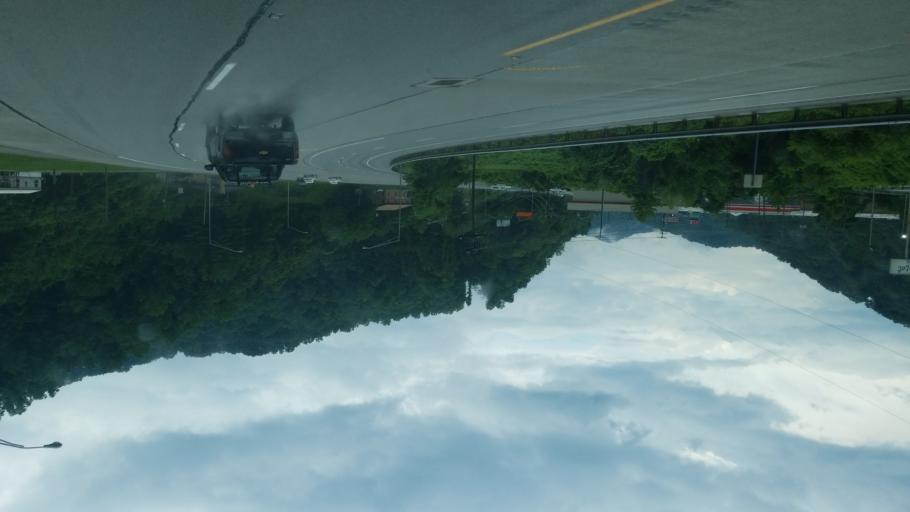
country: US
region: West Virginia
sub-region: Mingo County
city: Williamson
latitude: 37.6620
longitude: -82.2738
